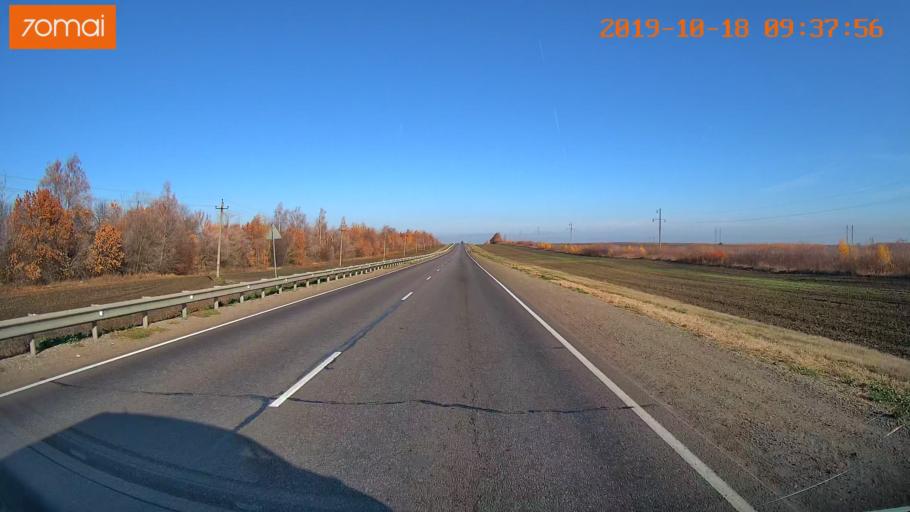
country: RU
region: Tula
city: Yefremov
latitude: 53.2302
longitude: 38.1390
